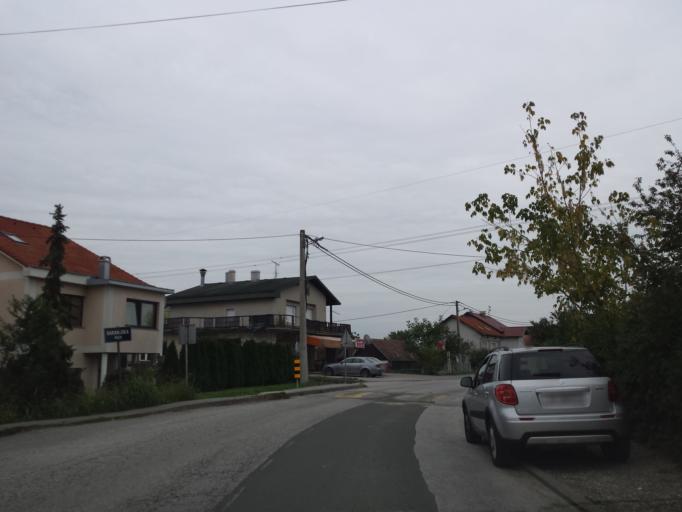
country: HR
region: Grad Zagreb
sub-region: Sesvete
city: Sesvete
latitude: 45.7981
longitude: 16.1193
